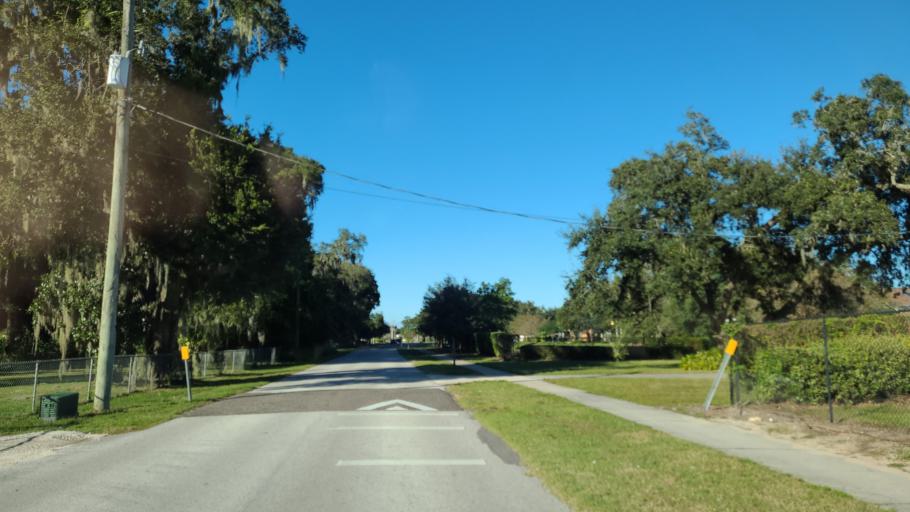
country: US
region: Florida
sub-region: Hillsborough County
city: Brandon
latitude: 27.9208
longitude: -82.2612
